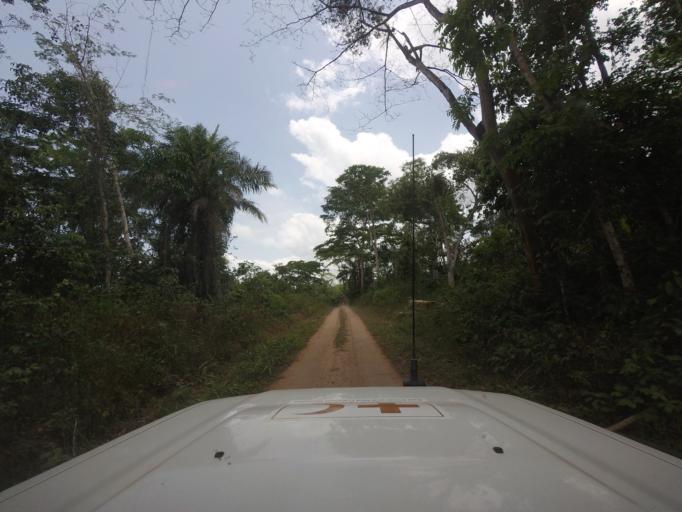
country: GN
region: Nzerekore
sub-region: Yomou
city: Yomou
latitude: 7.2757
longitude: -9.1861
